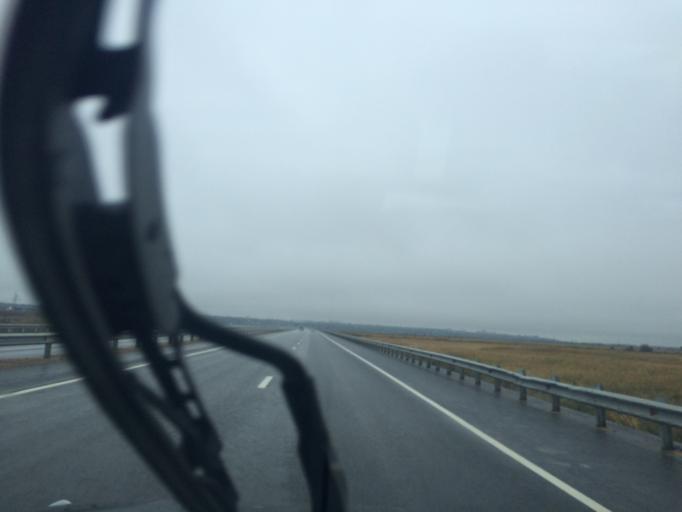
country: RU
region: Rostov
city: Kuleshovka
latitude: 47.0894
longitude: 39.5089
